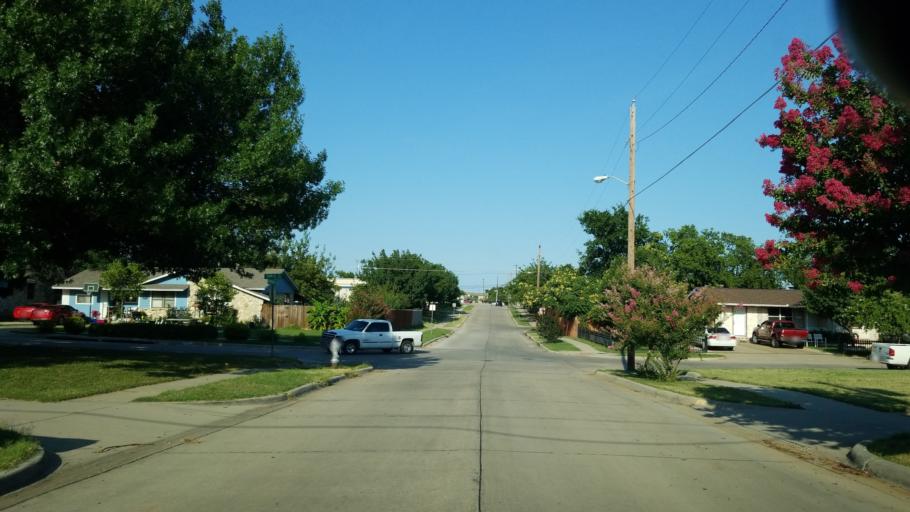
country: US
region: Texas
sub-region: Dallas County
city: Carrollton
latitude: 32.9415
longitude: -96.8929
